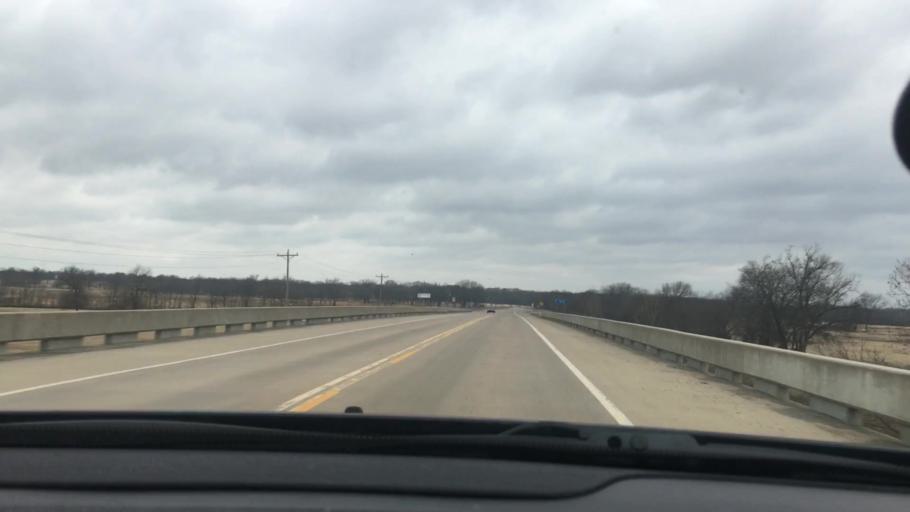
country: US
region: Oklahoma
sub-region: Atoka County
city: Atoka
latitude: 34.3696
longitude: -96.3210
